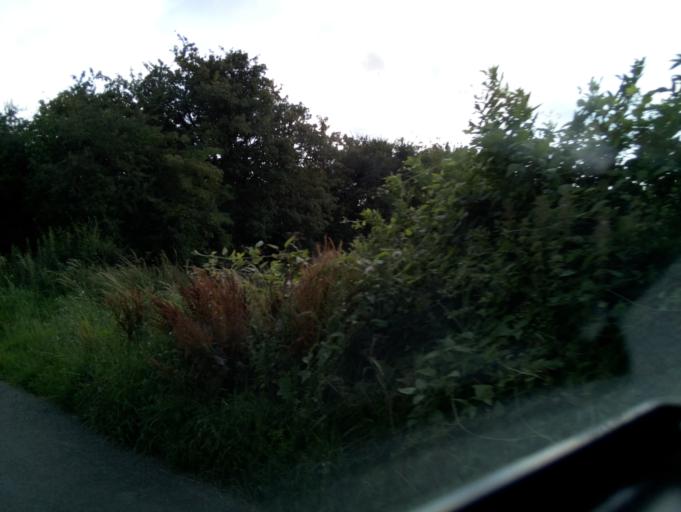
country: GB
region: England
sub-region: Gloucestershire
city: Tetbury
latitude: 51.6537
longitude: -2.1438
